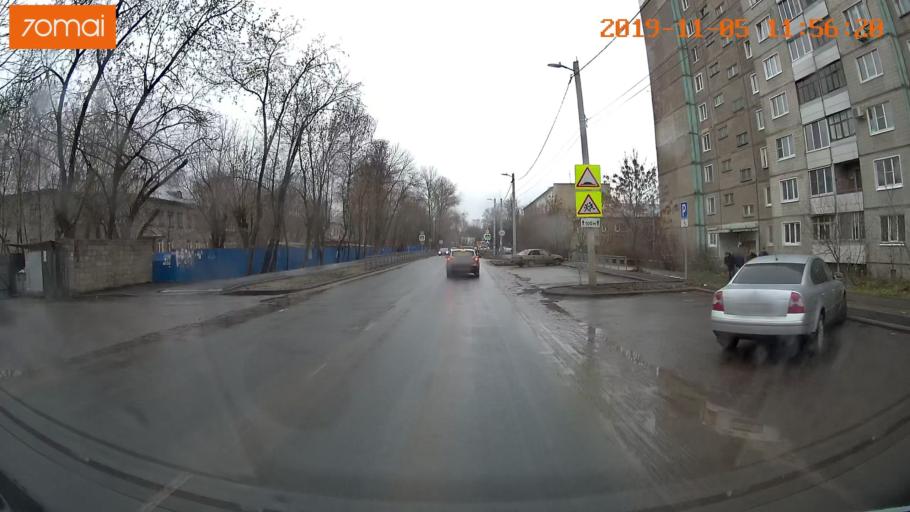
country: RU
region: Ivanovo
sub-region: Gorod Ivanovo
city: Ivanovo
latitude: 56.9863
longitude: 41.0302
